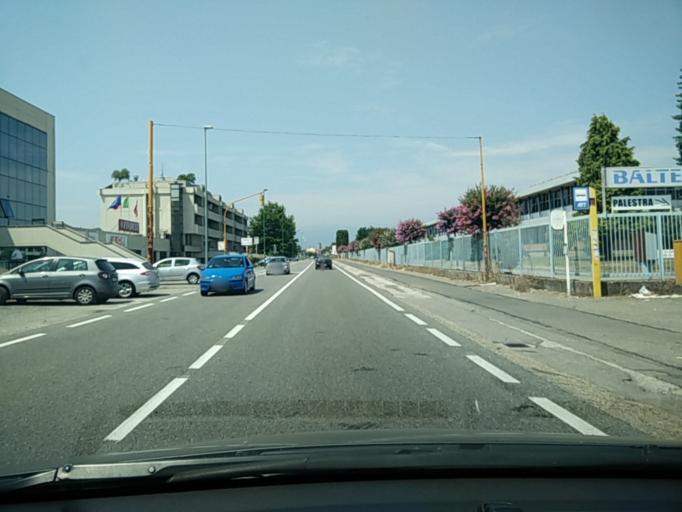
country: IT
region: Piedmont
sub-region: Provincia di Torino
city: Leini
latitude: 45.1847
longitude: 7.7309
